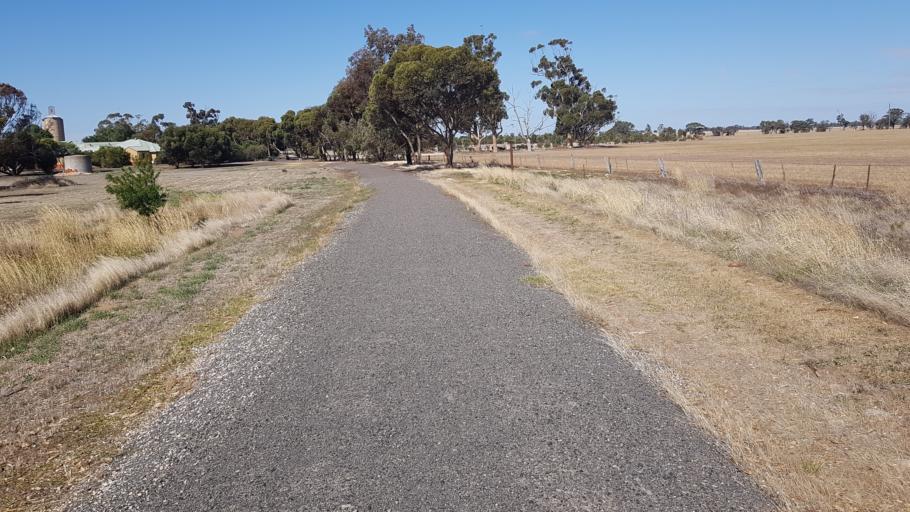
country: AU
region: Victoria
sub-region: Horsham
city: Horsham
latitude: -36.7465
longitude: 141.9354
